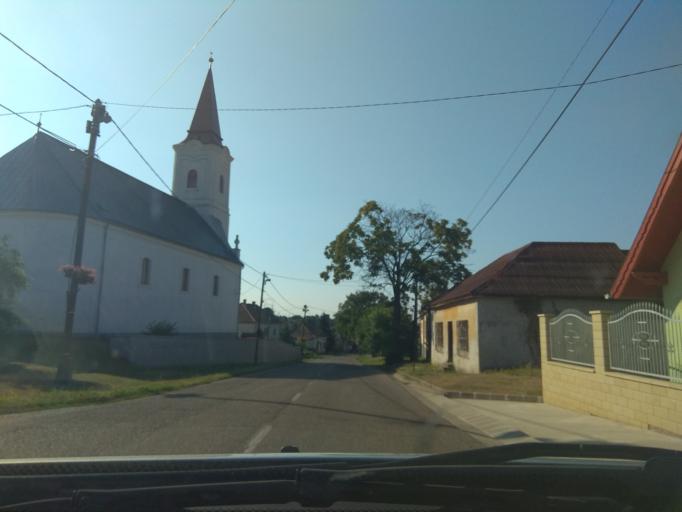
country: HU
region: Borsod-Abauj-Zemplen
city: Emod
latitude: 47.9451
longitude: 20.8130
